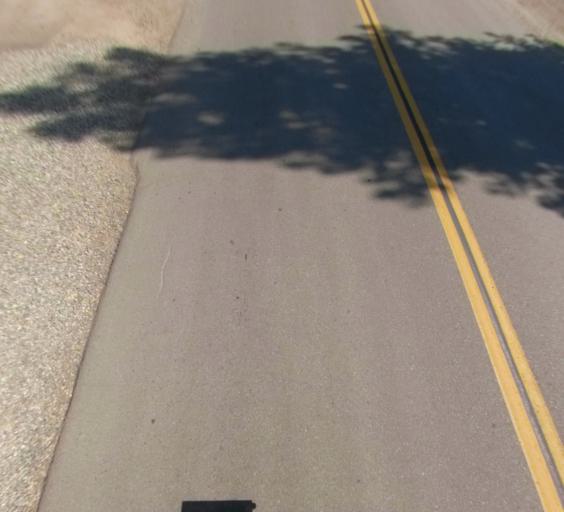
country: US
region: California
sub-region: Madera County
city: Bonadelle Ranchos-Madera Ranchos
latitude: 36.9007
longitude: -119.7995
